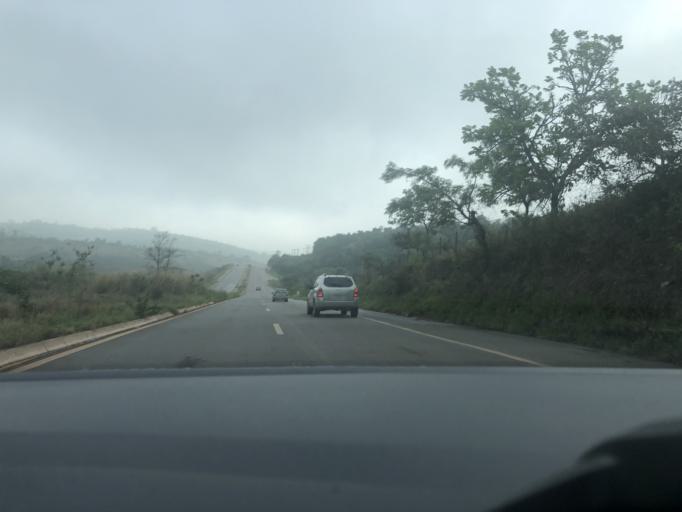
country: BR
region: Minas Gerais
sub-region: Congonhas
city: Congonhas
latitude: -20.5907
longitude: -43.9424
